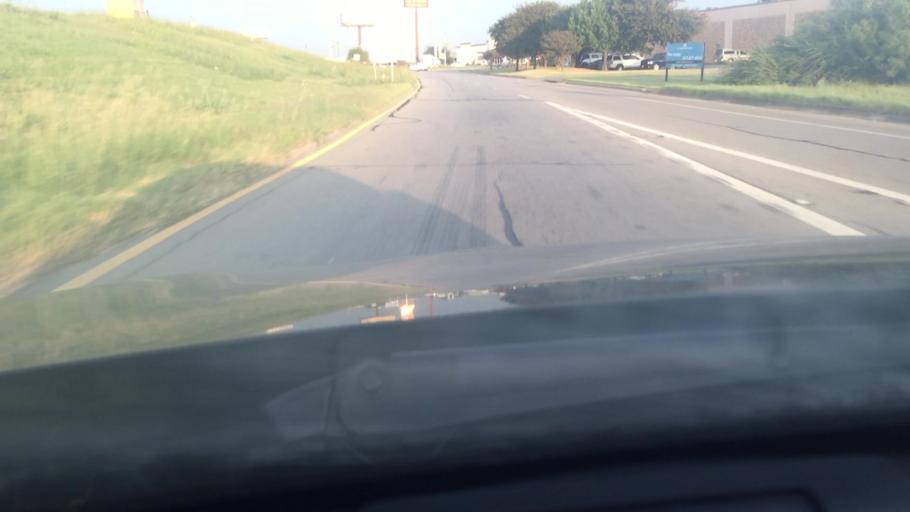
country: US
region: Texas
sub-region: Tarrant County
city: Blue Mound
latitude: 32.8430
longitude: -97.3404
